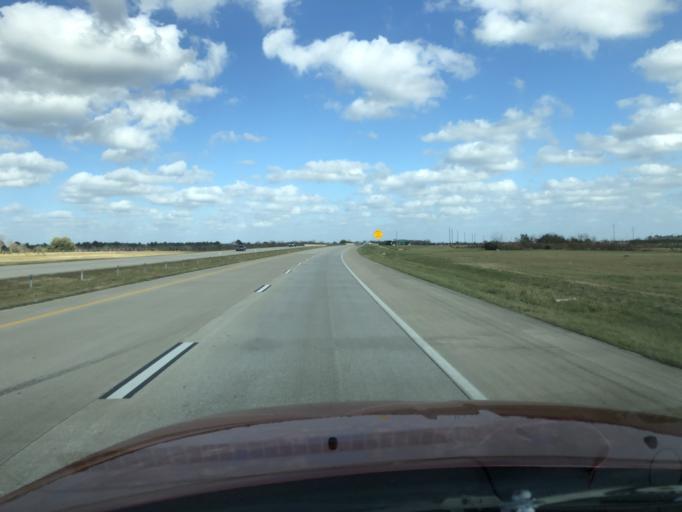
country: US
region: Texas
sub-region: Harris County
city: Cypress
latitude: 30.0493
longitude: -95.7508
